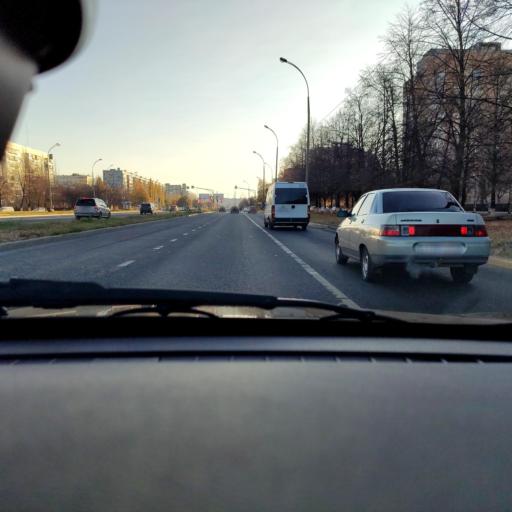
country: RU
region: Samara
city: Tol'yatti
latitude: 53.5266
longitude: 49.3070
